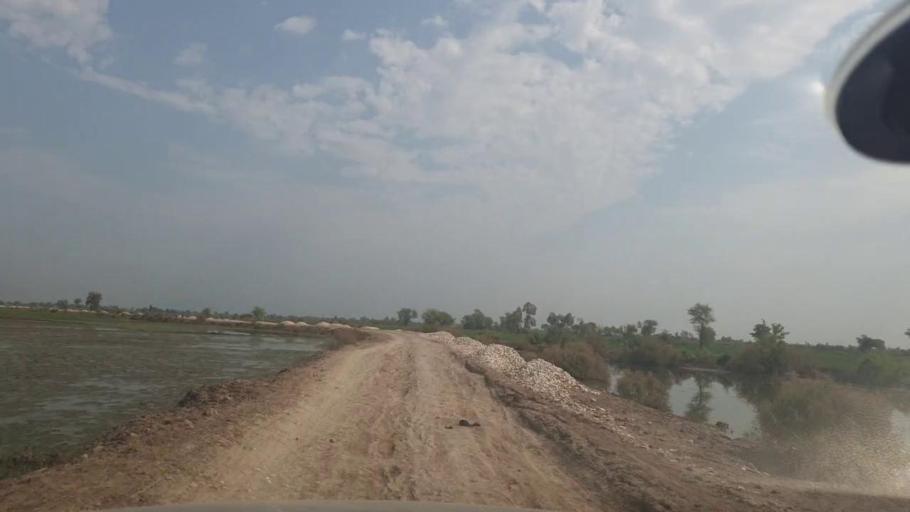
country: PK
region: Balochistan
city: Mehrabpur
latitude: 28.0761
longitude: 68.1007
